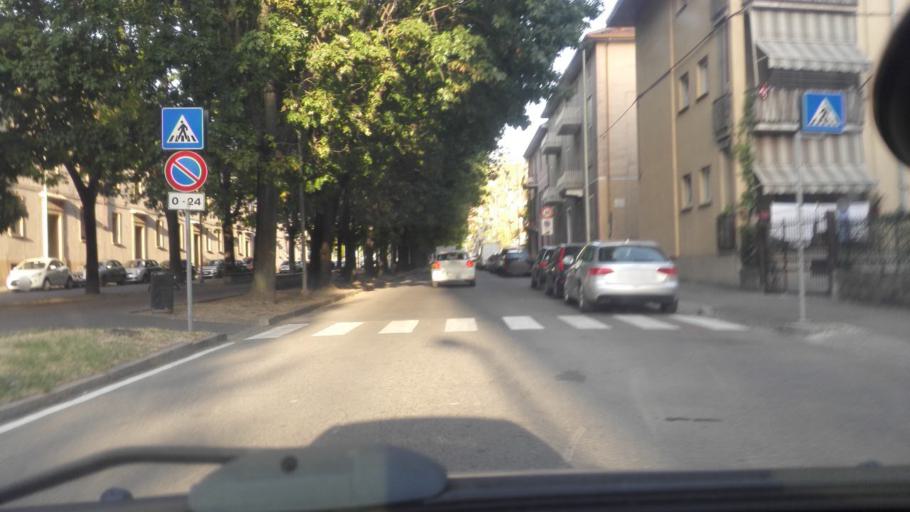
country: IT
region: Piedmont
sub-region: Provincia di Alessandria
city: Novi Ligure
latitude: 44.7674
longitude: 8.7881
